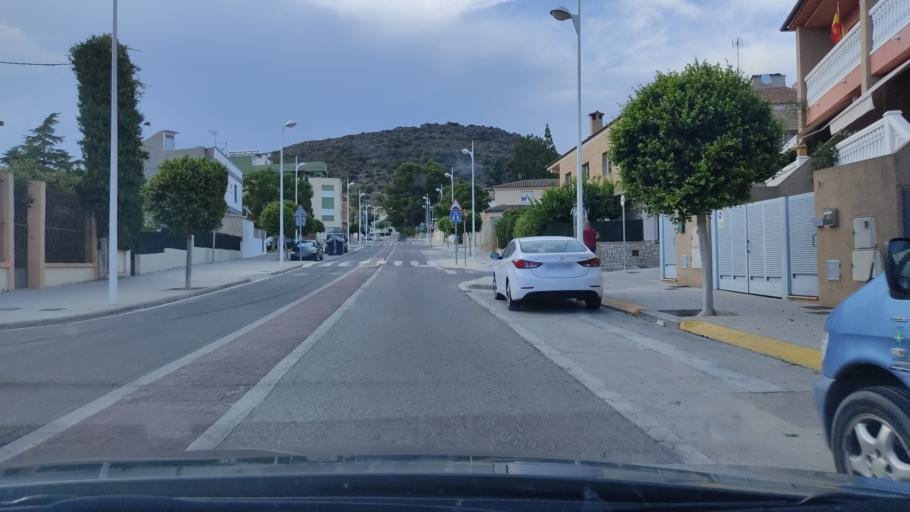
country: ES
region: Valencia
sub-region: Provincia de Valencia
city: Monserrat
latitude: 39.3591
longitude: -0.5986
